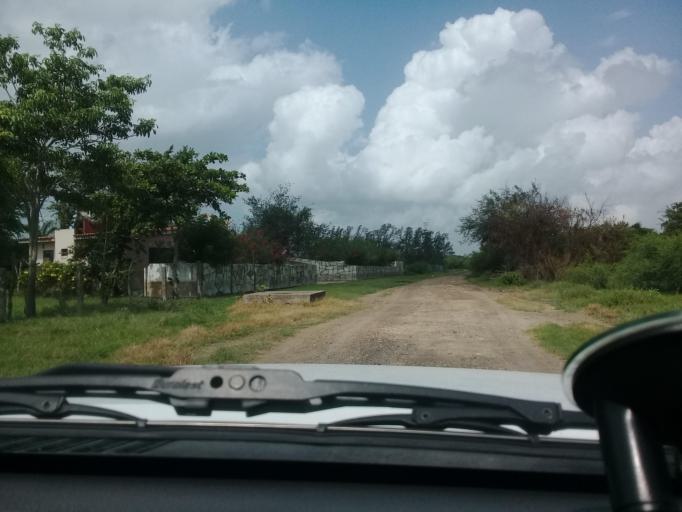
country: MX
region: Veracruz
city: Moralillo
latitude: 22.2121
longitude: -97.9562
